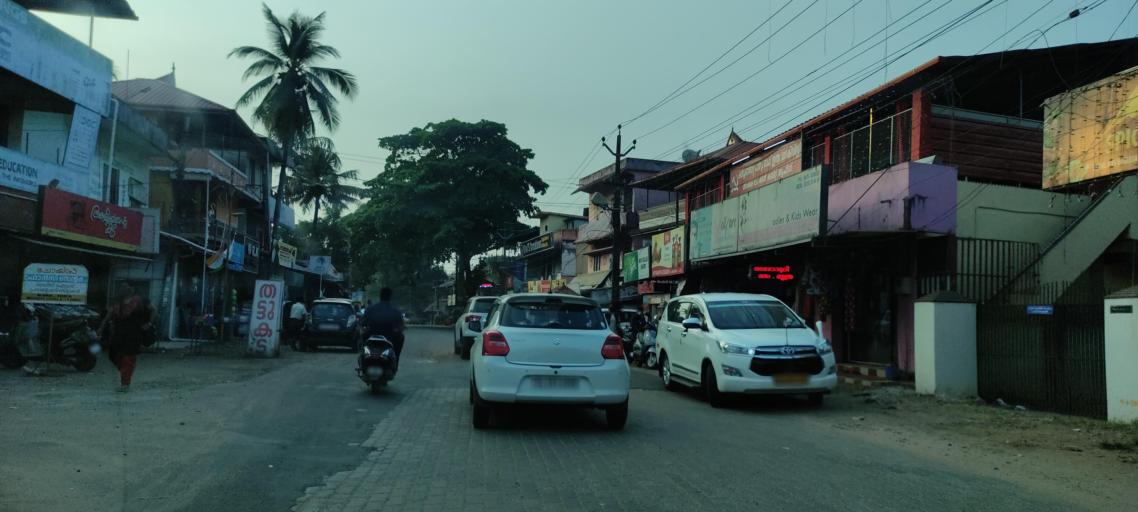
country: IN
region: Kerala
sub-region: Alappuzha
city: Mavelikara
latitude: 9.2556
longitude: 76.5582
